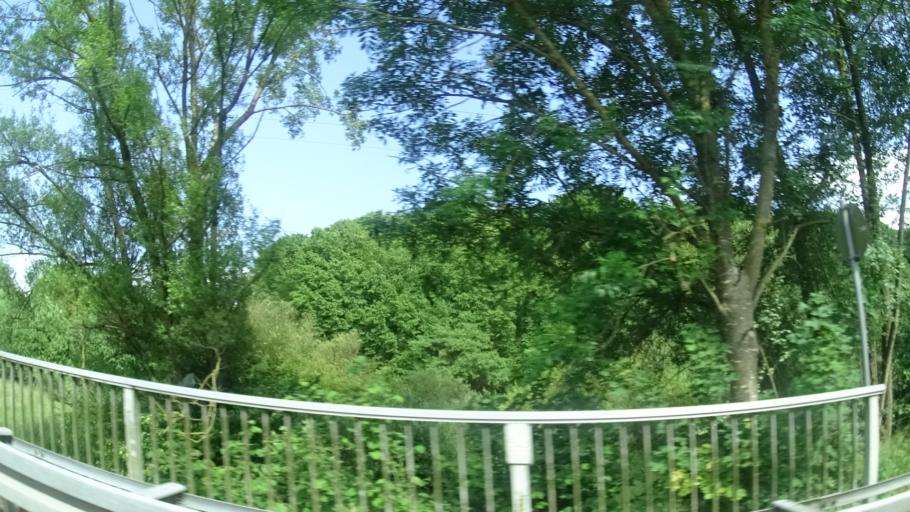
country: DE
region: Hesse
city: Haina
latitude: 51.0118
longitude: 8.9511
